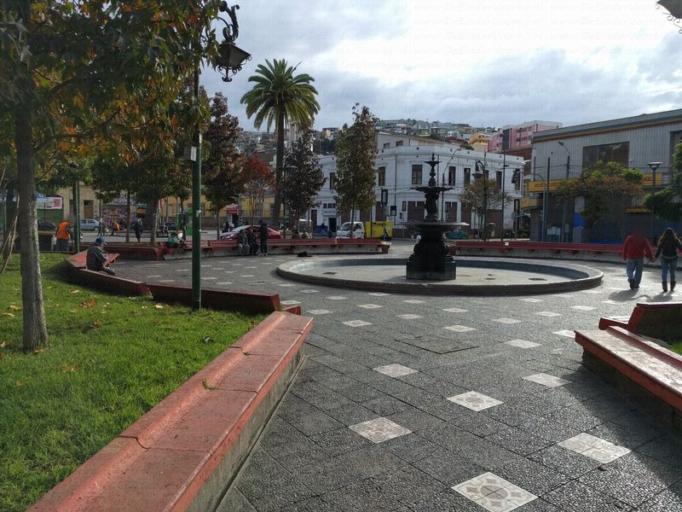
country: CL
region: Valparaiso
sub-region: Provincia de Valparaiso
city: Valparaiso
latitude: -33.0366
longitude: -71.6302
